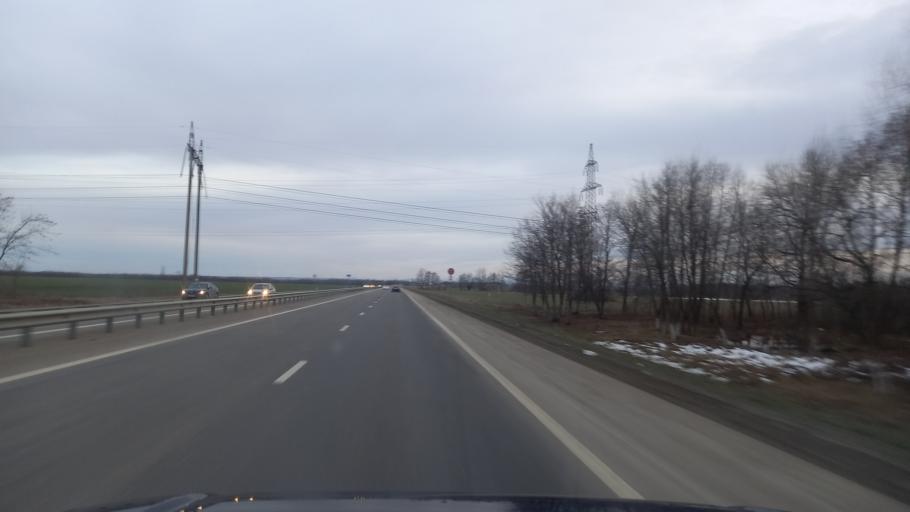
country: RU
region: Adygeya
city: Khanskaya
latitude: 44.7146
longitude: 39.9598
